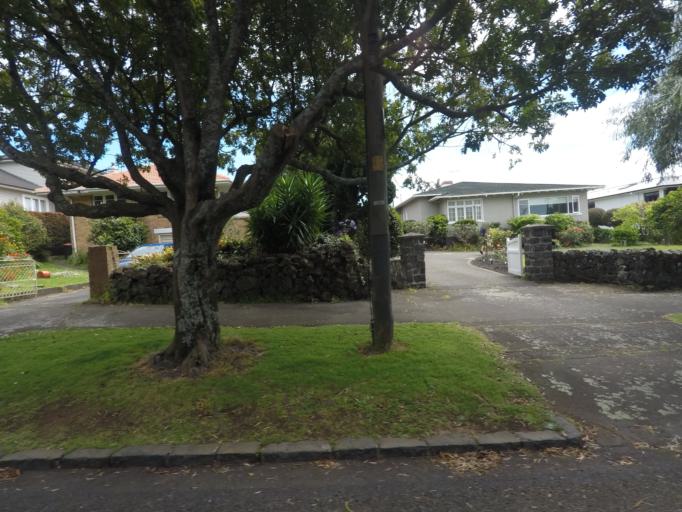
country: NZ
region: Auckland
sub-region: Auckland
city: Auckland
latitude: -36.8848
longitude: 174.7216
